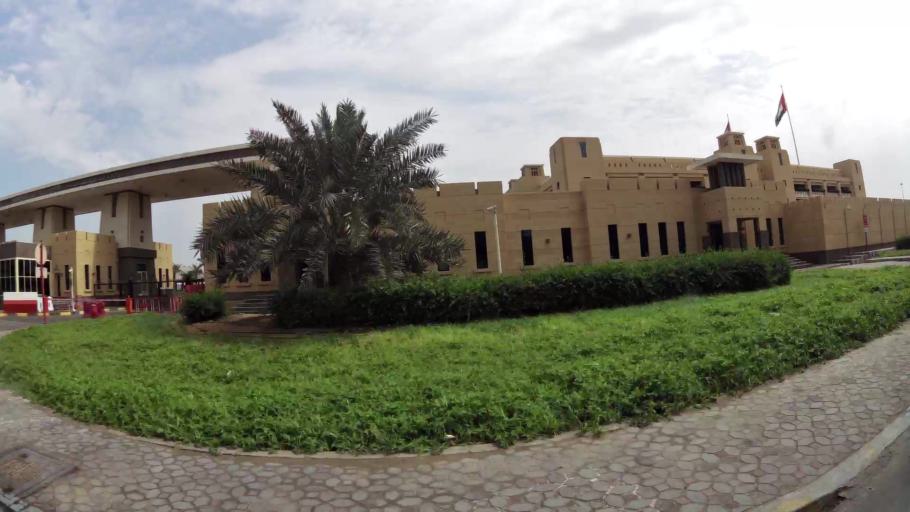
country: AE
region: Abu Dhabi
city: Abu Dhabi
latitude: 24.4122
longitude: 54.4637
